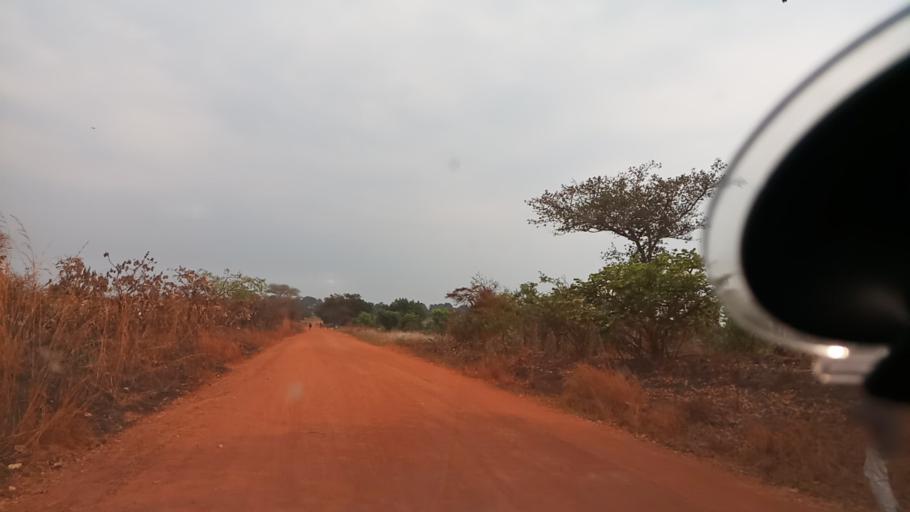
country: ZM
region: Luapula
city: Nchelenge
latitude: -9.1090
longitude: 28.3027
